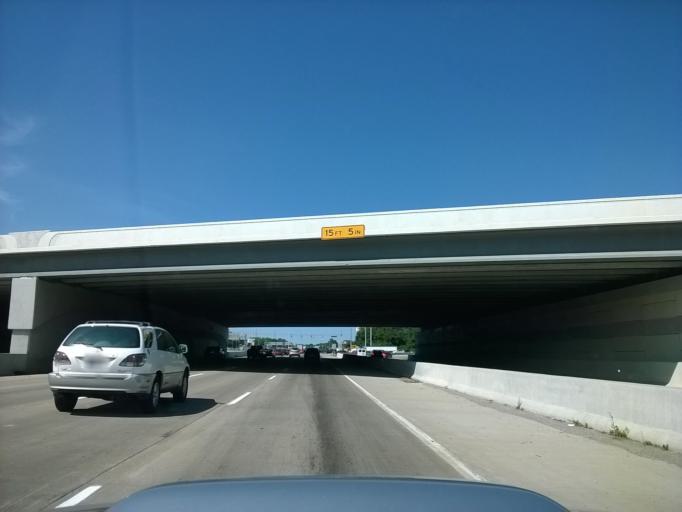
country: US
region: Indiana
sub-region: Marion County
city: Meridian Hills
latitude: 39.9206
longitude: -86.1120
